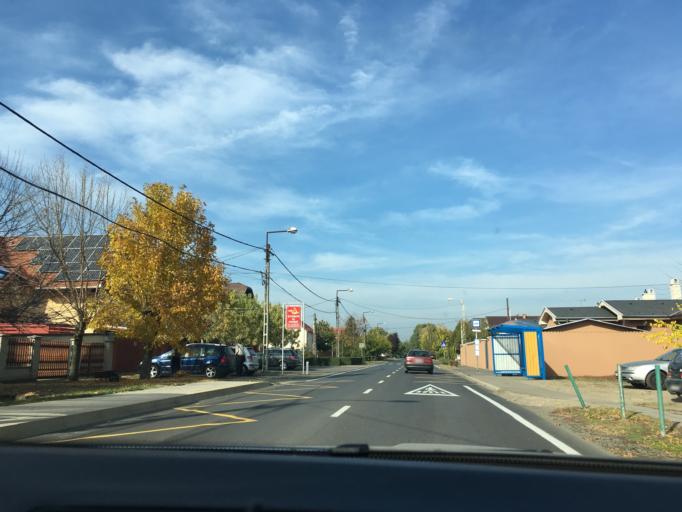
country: HU
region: Hajdu-Bihar
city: Debrecen
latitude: 47.5416
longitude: 21.6714
